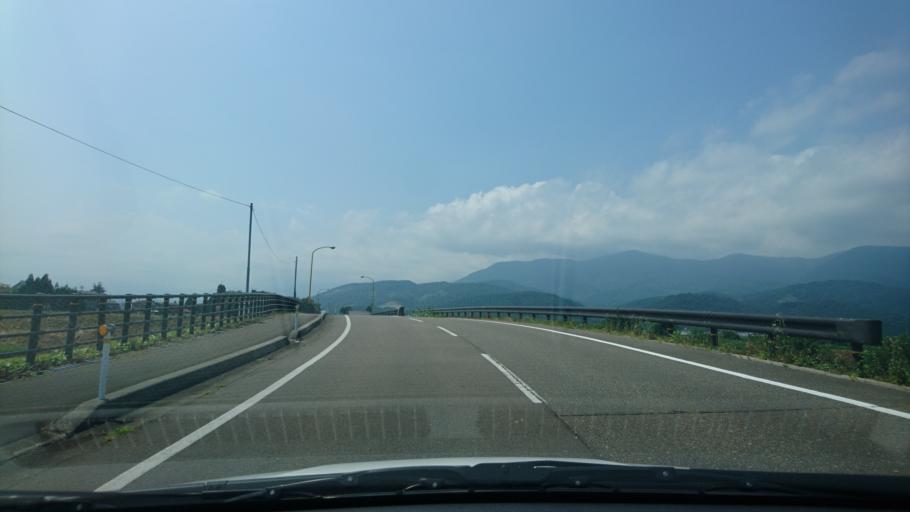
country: JP
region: Niigata
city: Arai
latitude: 37.0530
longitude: 138.2542
